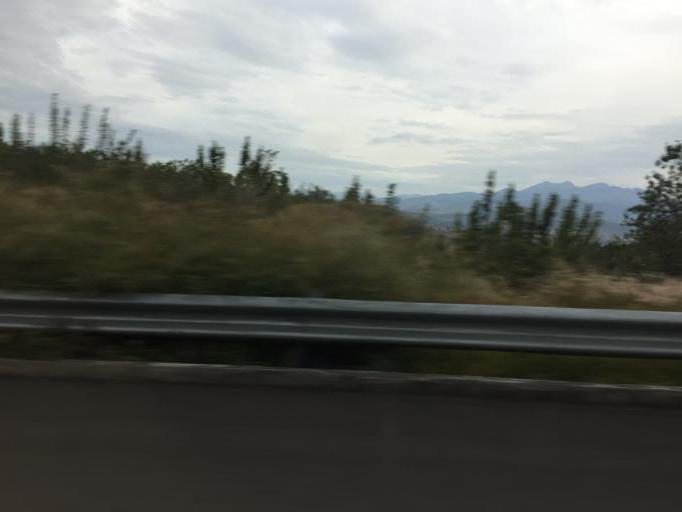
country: MX
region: Mexico
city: Huaniqueo de Morales
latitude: 19.8868
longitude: -101.4699
